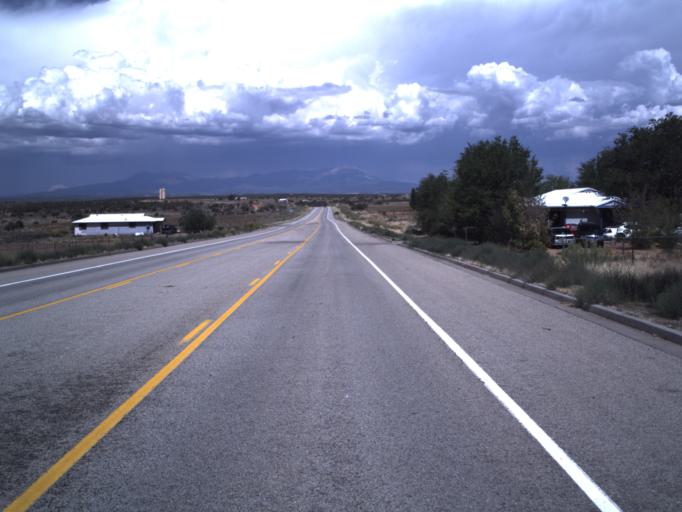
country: US
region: Utah
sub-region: San Juan County
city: Blanding
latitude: 37.4669
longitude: -109.4669
